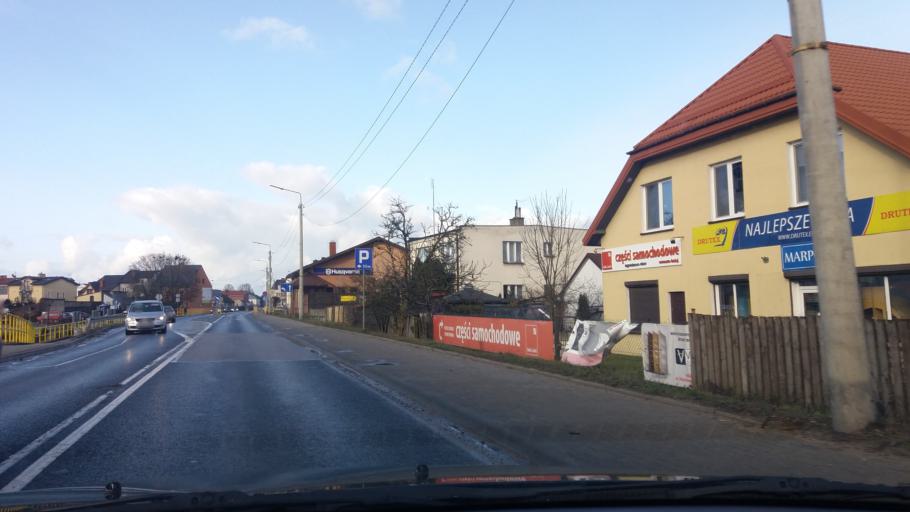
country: PL
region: Masovian Voivodeship
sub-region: Powiat przasnyski
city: Chorzele
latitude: 53.2564
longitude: 20.8973
